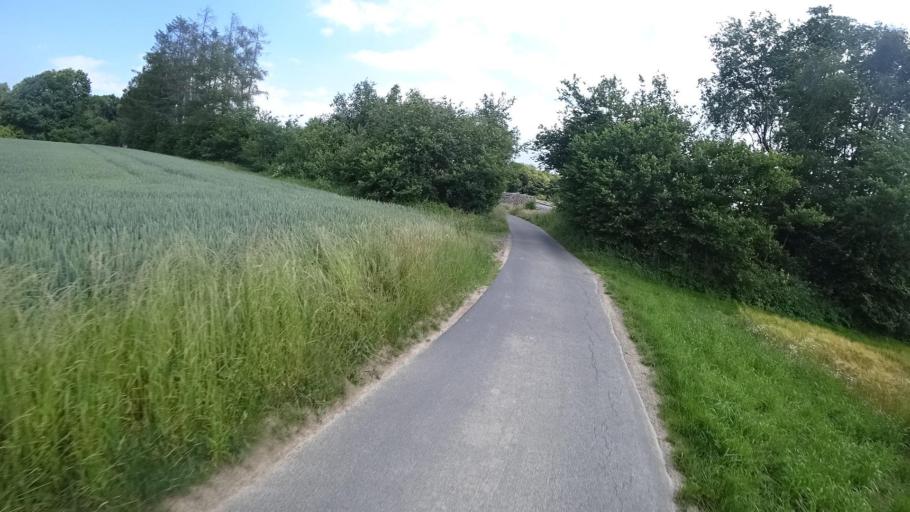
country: DE
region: Rheinland-Pfalz
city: Heupelzen
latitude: 50.7084
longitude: 7.6108
